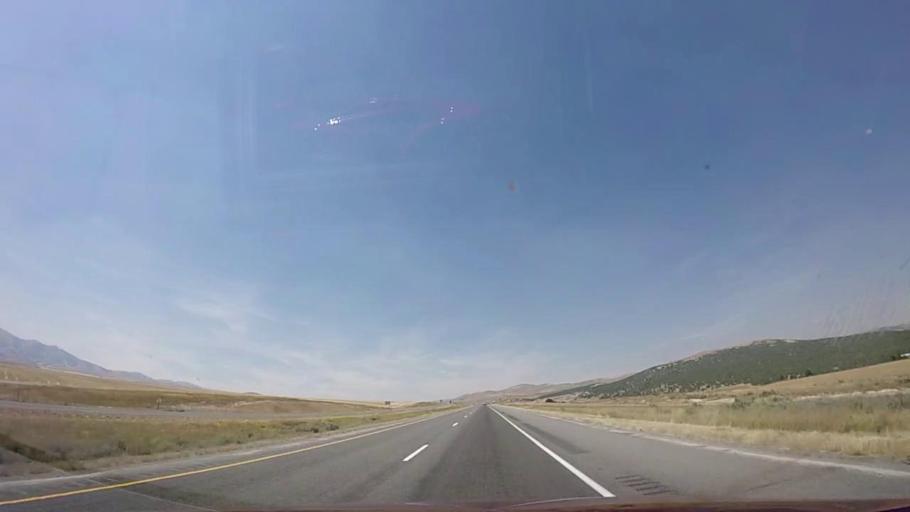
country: US
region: Idaho
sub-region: Power County
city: American Falls
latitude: 42.1524
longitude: -112.9854
